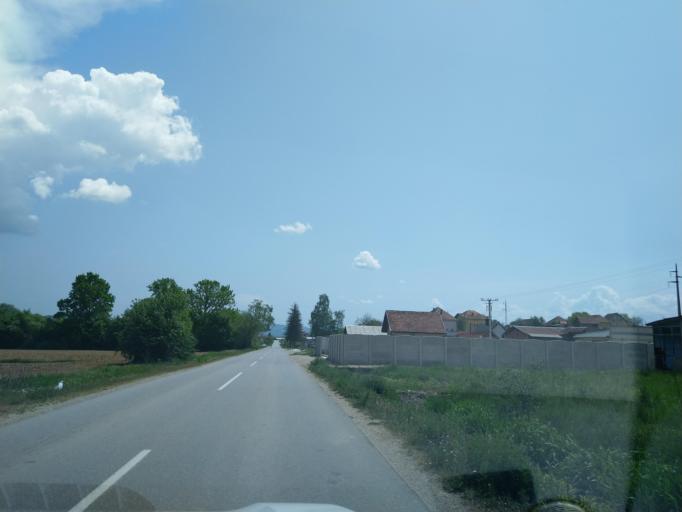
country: RS
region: Central Serbia
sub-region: Zlatiborski Okrug
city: Pozega
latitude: 43.8540
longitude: 19.9912
